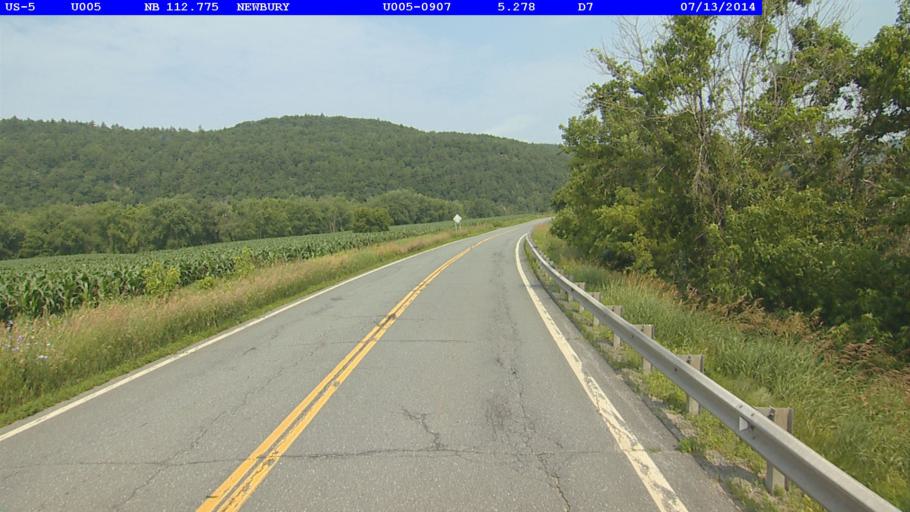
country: US
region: New Hampshire
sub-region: Grafton County
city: North Haverhill
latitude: 44.0976
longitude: -72.0500
